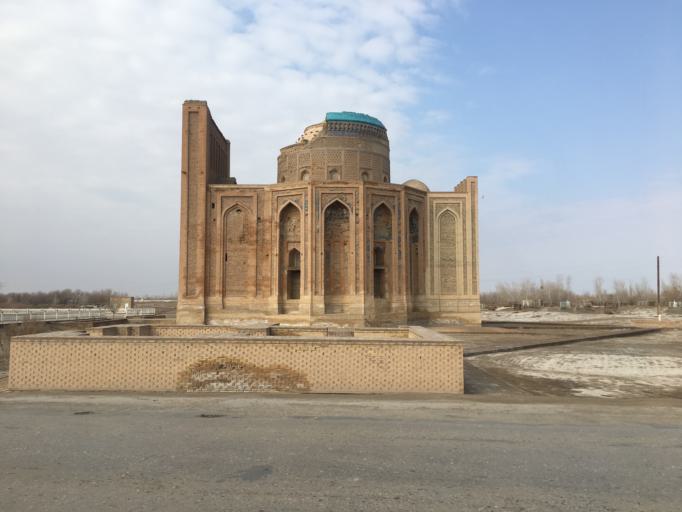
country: TM
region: Dasoguz
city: Koeneuergench
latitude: 42.3112
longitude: 59.1378
